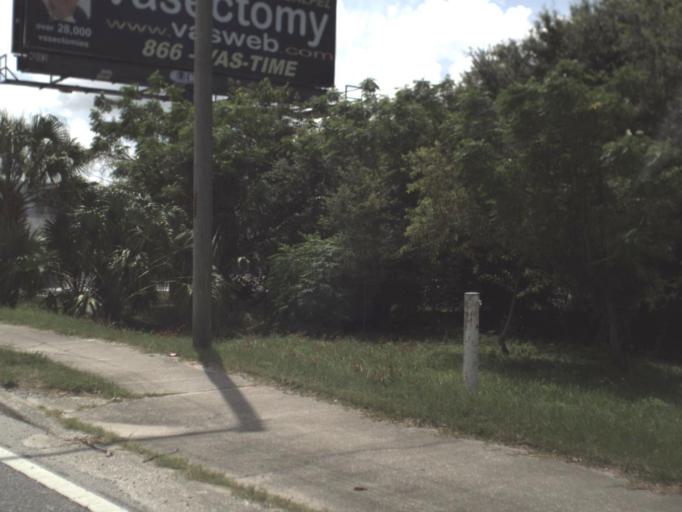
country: US
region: Florida
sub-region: Pasco County
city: Bayonet Point
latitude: 28.3303
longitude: -82.6521
